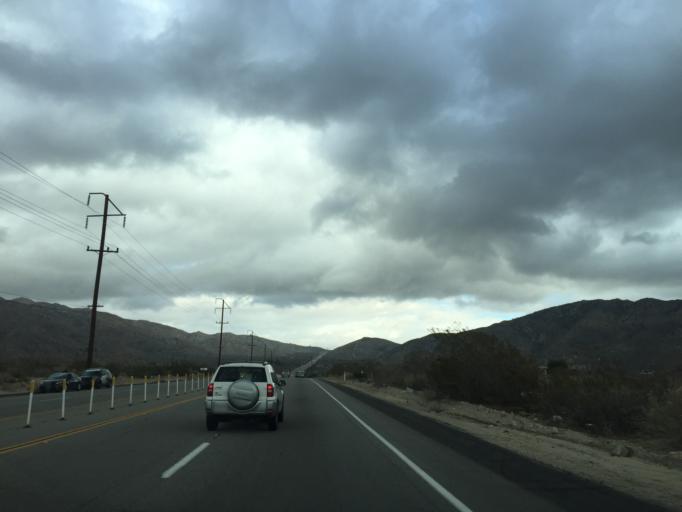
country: US
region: California
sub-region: San Bernardino County
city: Morongo Valley
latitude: 34.0876
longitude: -116.5227
